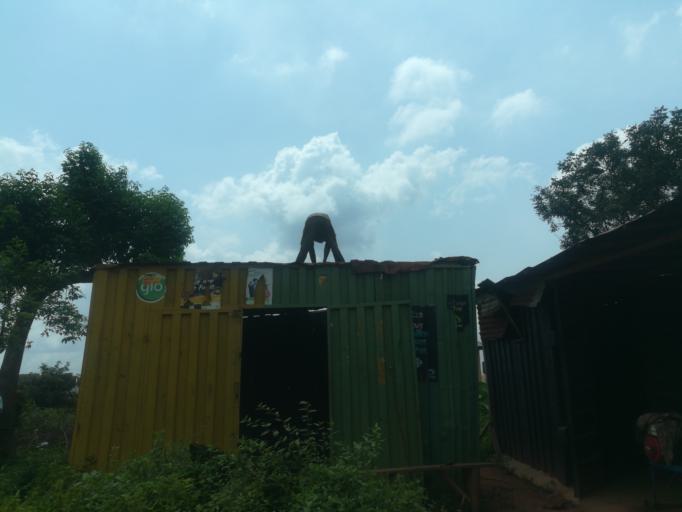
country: NG
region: Oyo
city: Moniya
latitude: 7.4665
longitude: 3.9610
